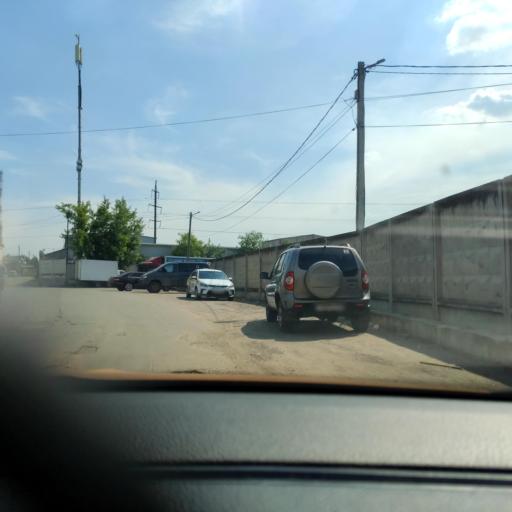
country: RU
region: Moscow
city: Severnyy
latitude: 55.9588
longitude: 37.5433
